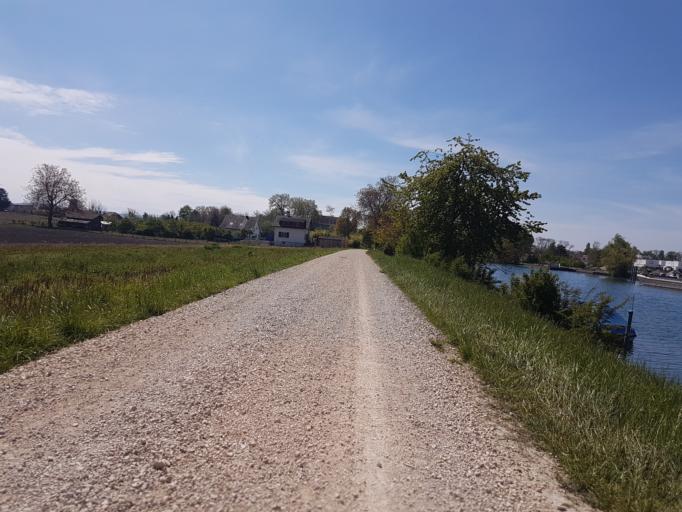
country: CH
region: Neuchatel
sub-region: Neuchatel District
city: Cornaux
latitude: 47.0252
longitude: 7.0339
